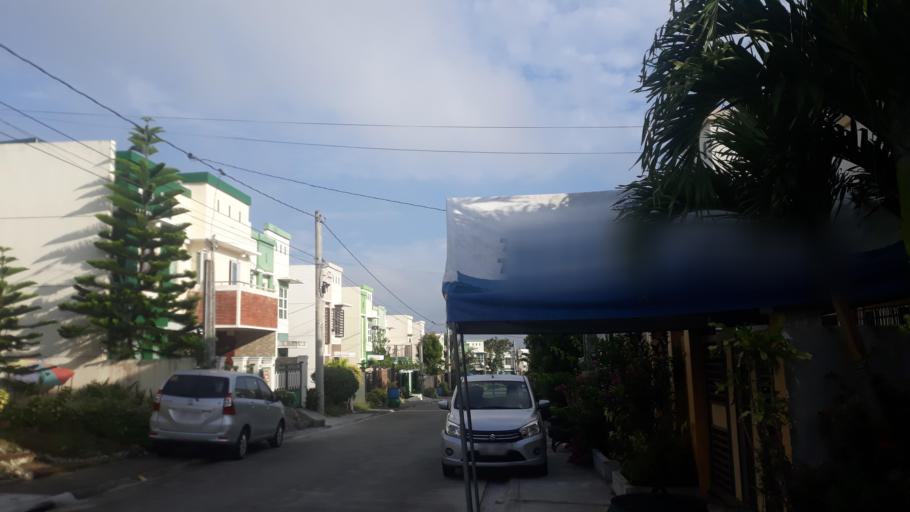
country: PH
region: Calabarzon
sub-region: Province of Cavite
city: Biga
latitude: 14.2744
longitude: 120.9688
